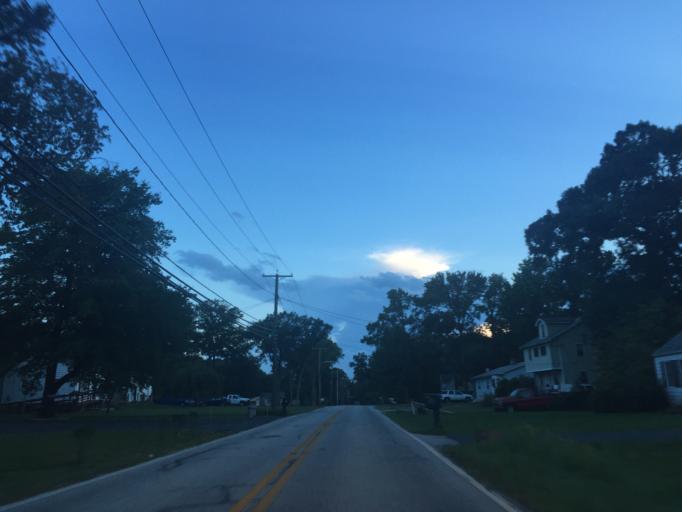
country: US
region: Maryland
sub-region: Baltimore County
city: Bowleys Quarters
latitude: 39.3672
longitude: -76.3628
